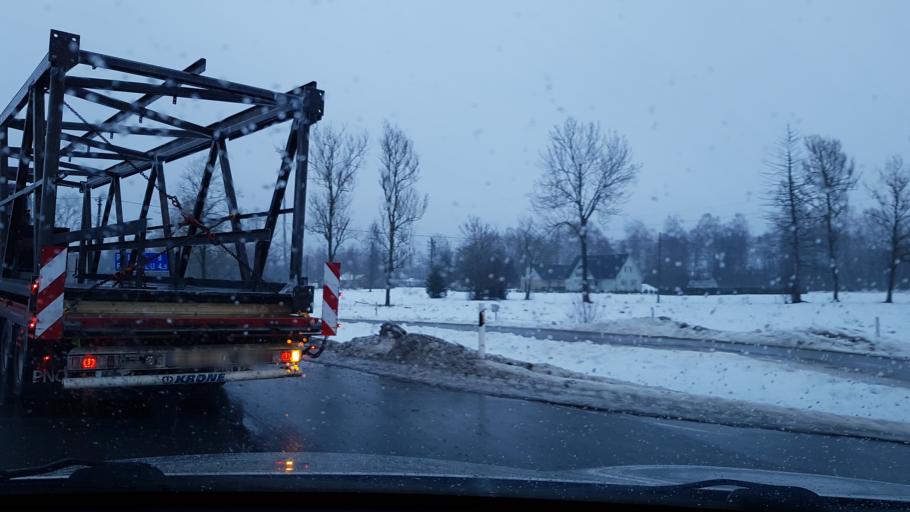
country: EE
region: Jaervamaa
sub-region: Tueri vald
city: Tueri
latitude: 58.8474
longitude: 25.4790
